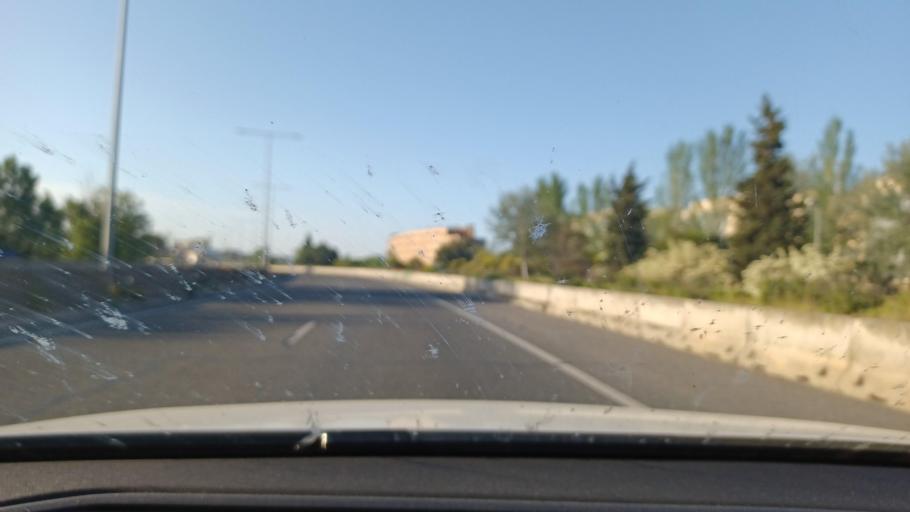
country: ES
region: Castille and Leon
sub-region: Provincia de Valladolid
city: Cisterniga
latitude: 41.6190
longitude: -4.7158
